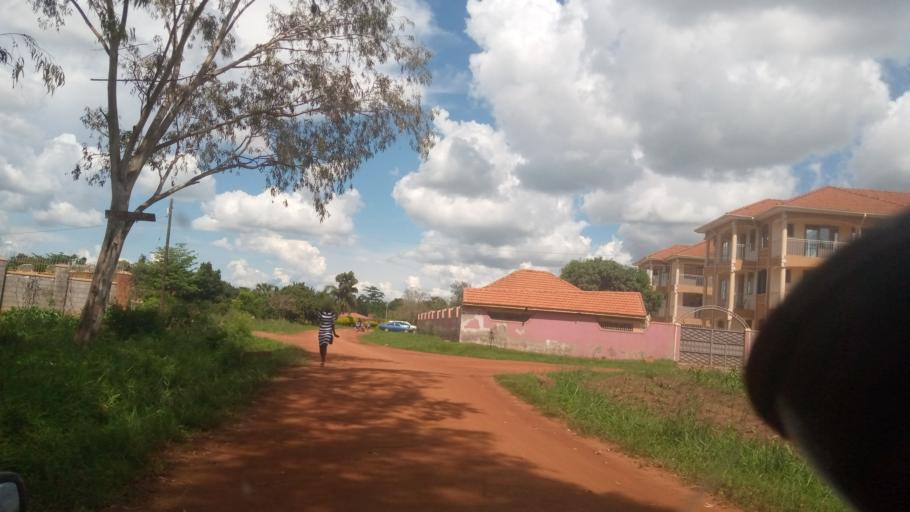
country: UG
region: Northern Region
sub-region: Lira District
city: Lira
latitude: 2.2383
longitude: 32.9052
